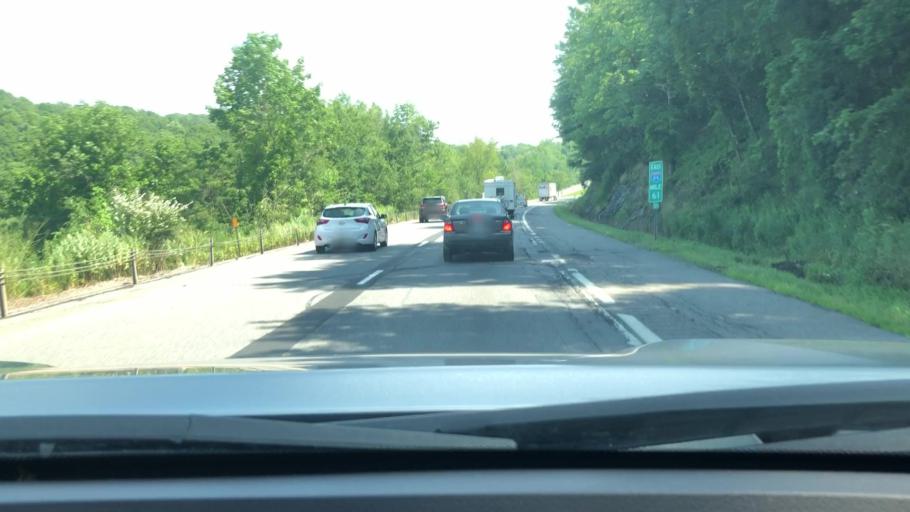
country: US
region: New York
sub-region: Putnam County
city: Lake Carmel
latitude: 41.4846
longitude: -73.6569
